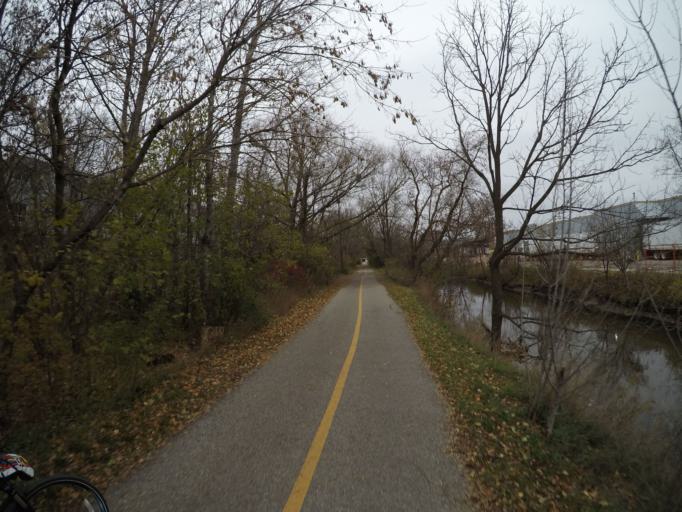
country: CA
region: Ontario
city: Waterloo
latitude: 43.4705
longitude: -80.5171
